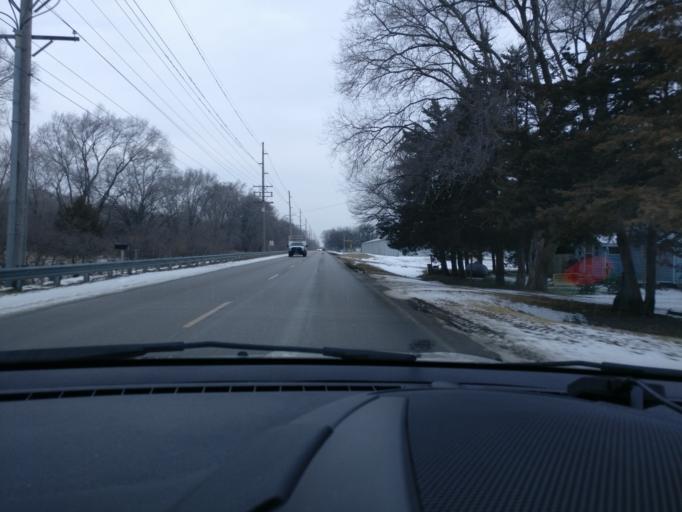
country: US
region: Nebraska
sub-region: Dodge County
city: Fremont
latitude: 41.4385
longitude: -96.5234
